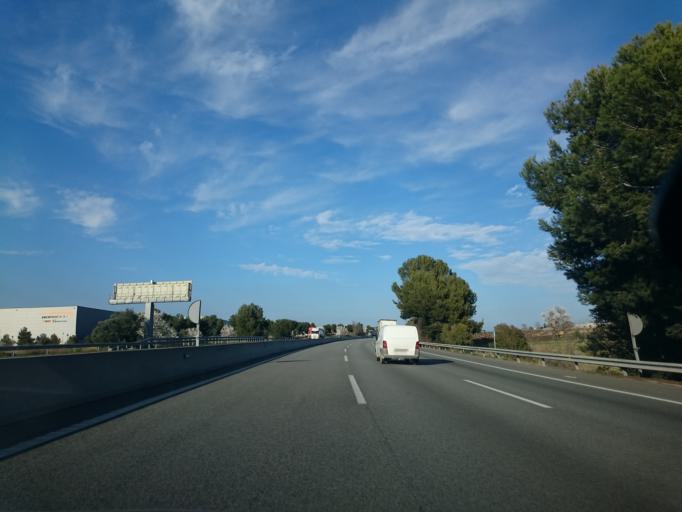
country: ES
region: Catalonia
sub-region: Provincia de Barcelona
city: La Granada
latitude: 41.3692
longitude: 1.7278
